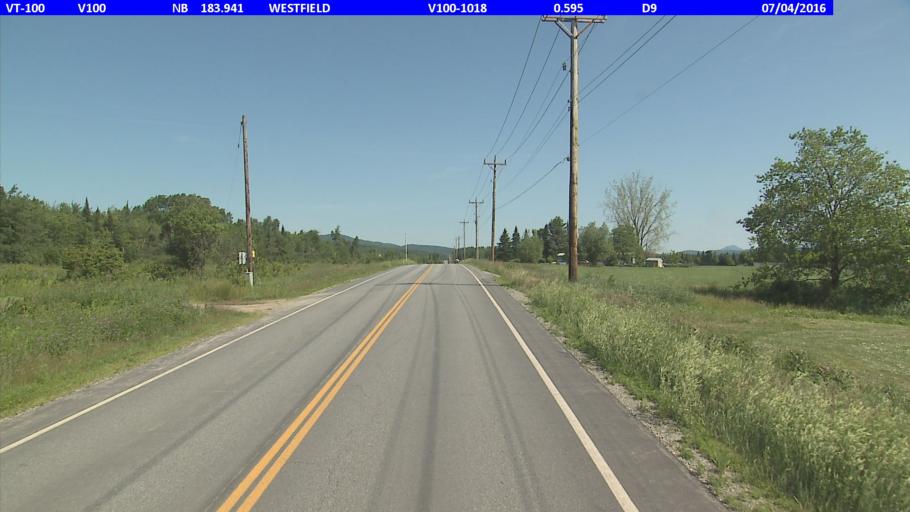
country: US
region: Vermont
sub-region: Orleans County
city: Newport
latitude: 44.8435
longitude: -72.4339
